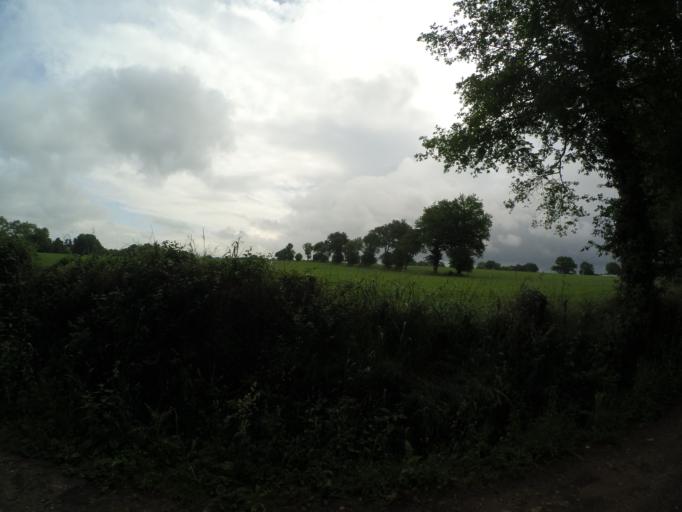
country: FR
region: Pays de la Loire
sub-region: Departement de la Vendee
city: Nesmy
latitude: 46.6102
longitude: -1.3958
